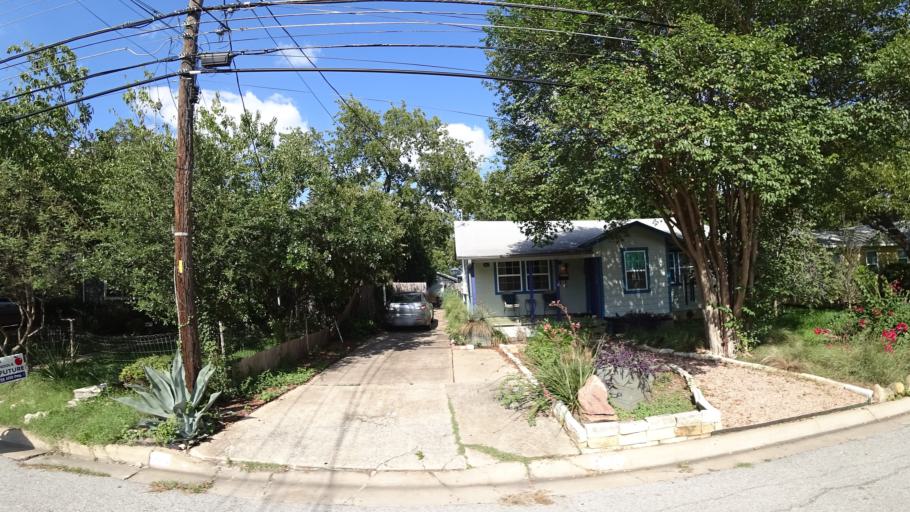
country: US
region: Texas
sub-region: Travis County
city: Austin
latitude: 30.3139
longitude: -97.7121
